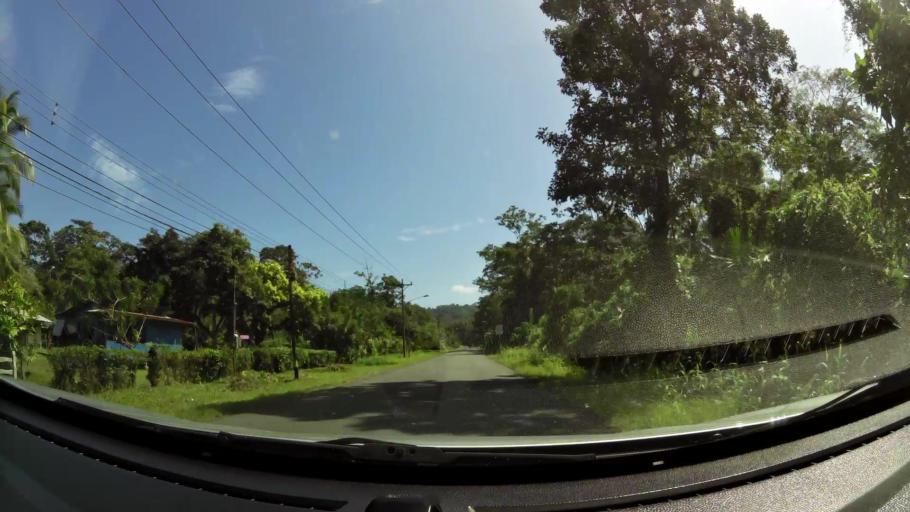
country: PA
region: Bocas del Toro
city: Barranco
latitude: 9.6512
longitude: -82.7935
